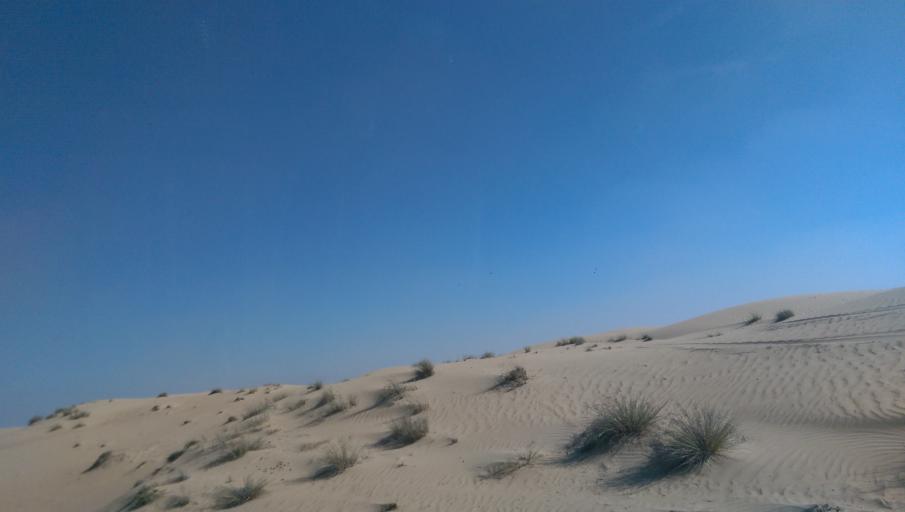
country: AE
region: Dubai
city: Dubai
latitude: 24.9641
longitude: 55.3478
